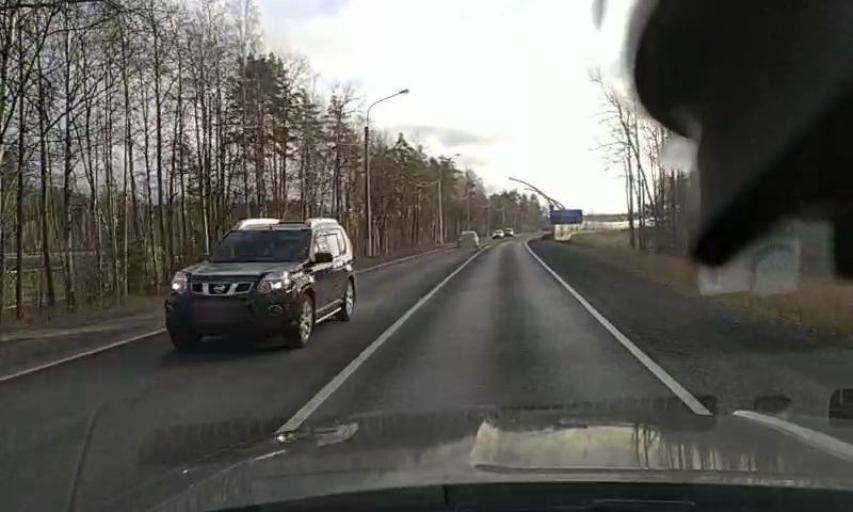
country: RU
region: St.-Petersburg
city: Solnechnoye
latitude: 60.1538
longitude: 29.9643
